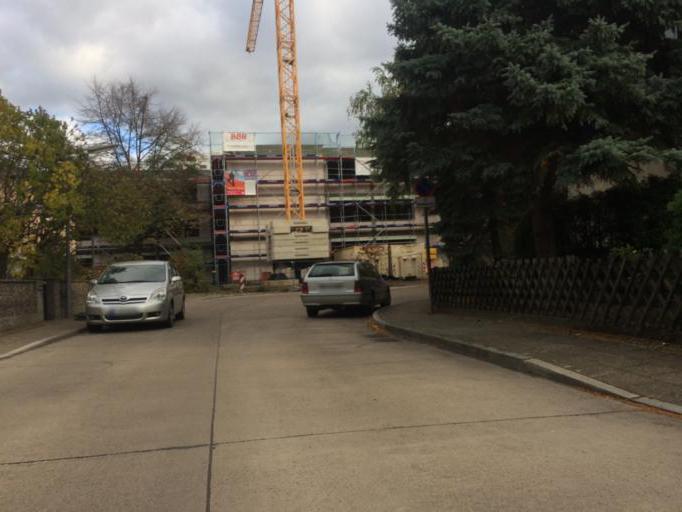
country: DE
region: Berlin
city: Markisches Viertel
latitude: 52.5952
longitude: 13.3585
